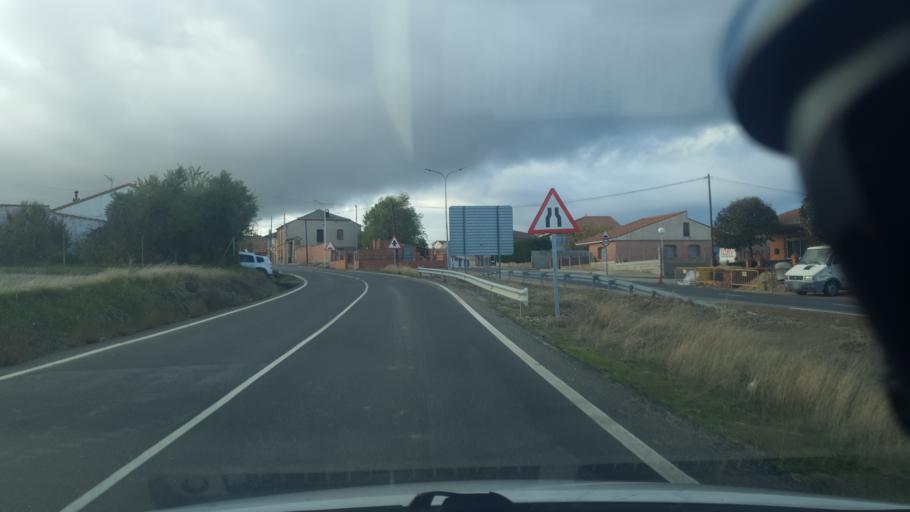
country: ES
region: Castille and Leon
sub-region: Provincia de Segovia
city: Santiuste de San Juan Bautista
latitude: 41.1549
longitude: -4.5683
